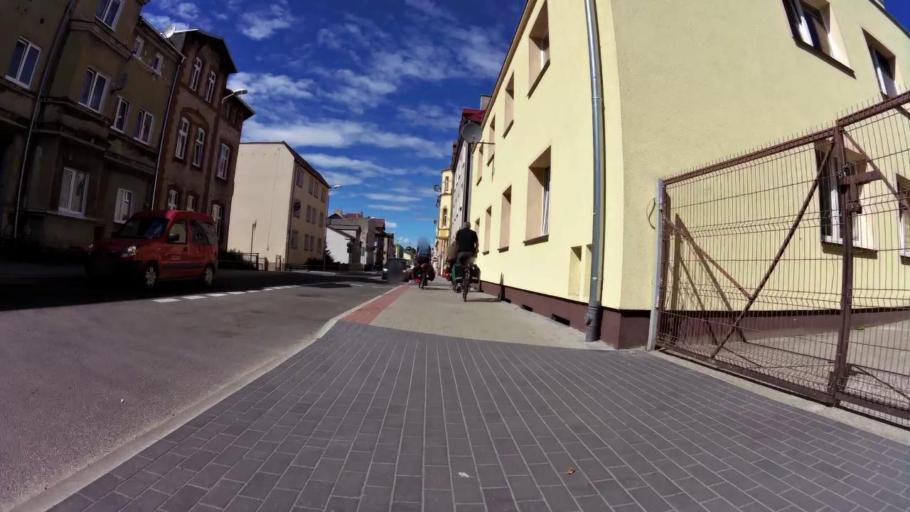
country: PL
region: West Pomeranian Voivodeship
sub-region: Powiat swidwinski
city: Swidwin
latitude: 53.7777
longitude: 15.7725
